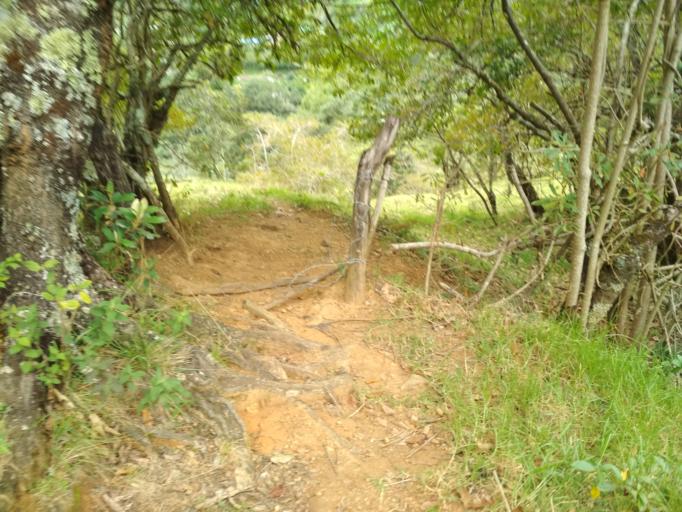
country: CO
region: Cauca
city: Totoro
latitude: 2.5318
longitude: -76.4216
